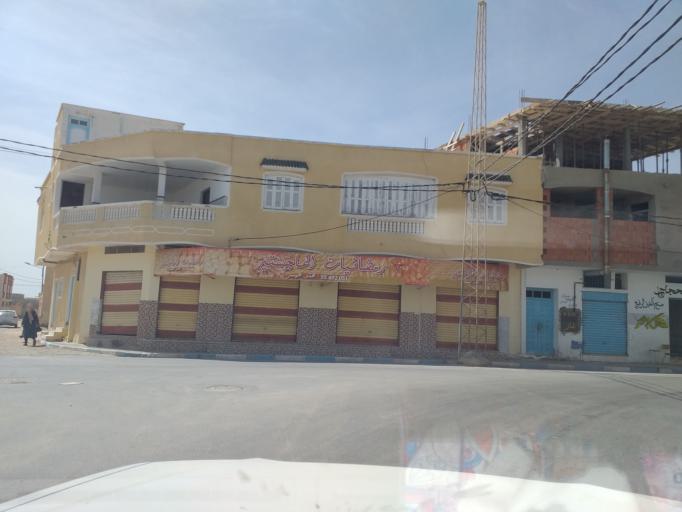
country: TN
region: Qabis
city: Gabes
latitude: 33.9414
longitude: 10.0682
